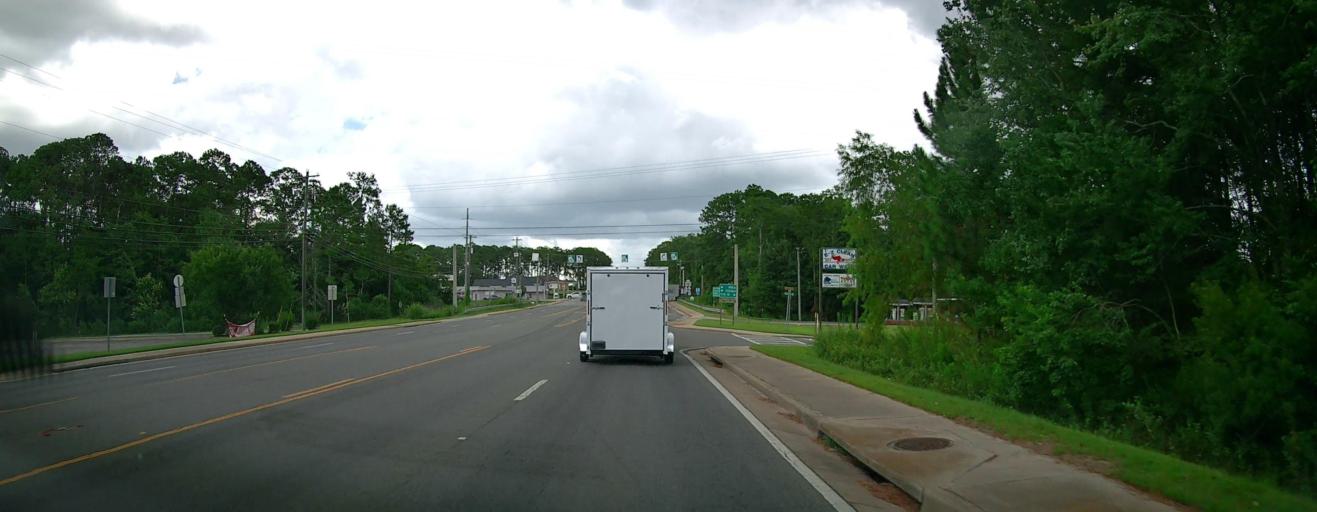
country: US
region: Georgia
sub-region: Coffee County
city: Douglas
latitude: 31.5133
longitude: -82.8731
